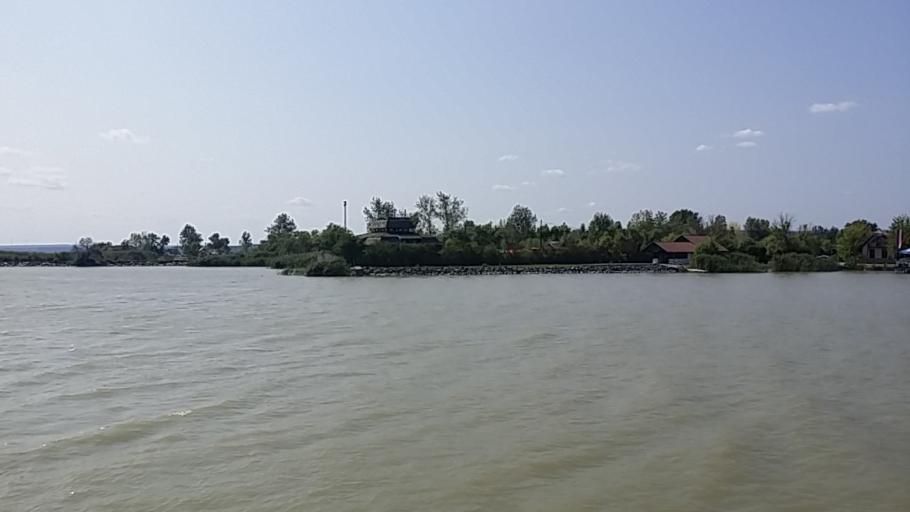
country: AT
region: Burgenland
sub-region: Eisenstadt-Umgebung
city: Morbisch am See
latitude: 47.7215
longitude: 16.6941
